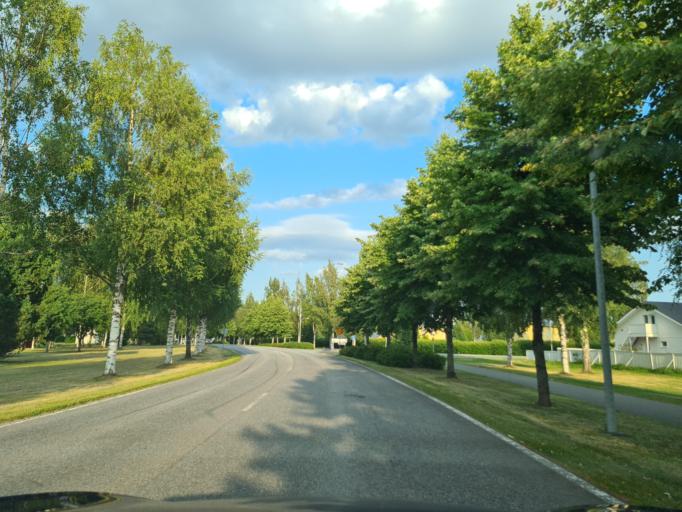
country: FI
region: Southern Ostrobothnia
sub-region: Seinaejoki
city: Lapua
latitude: 62.9684
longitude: 22.9825
